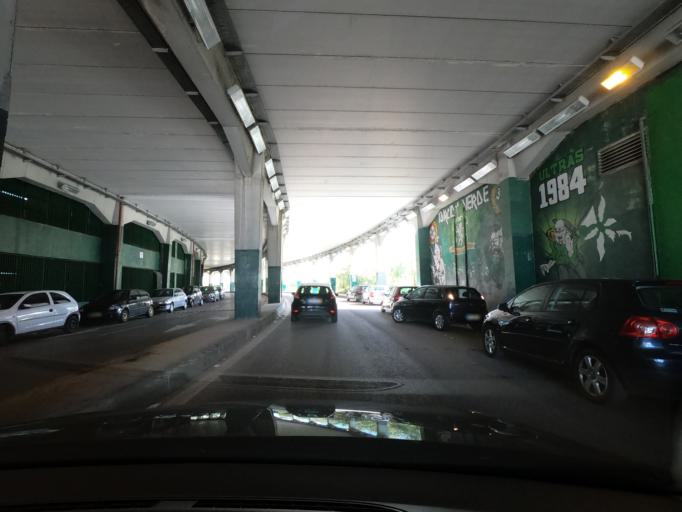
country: PT
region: Lisbon
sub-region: Odivelas
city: Olival do Basto
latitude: 38.7606
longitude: -9.1593
